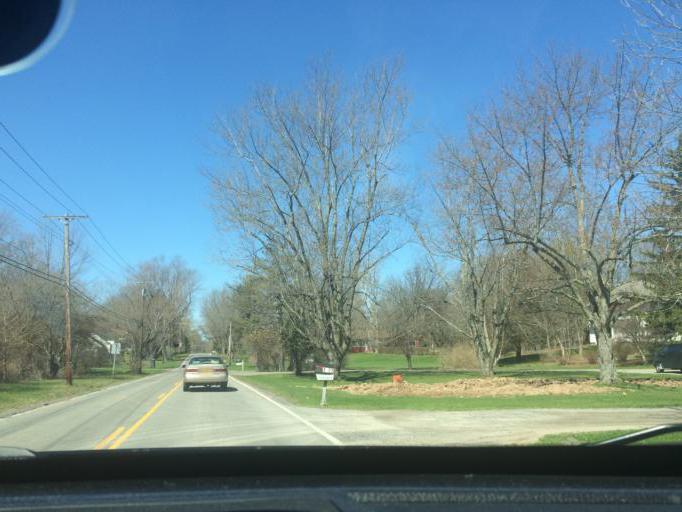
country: US
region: New York
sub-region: Monroe County
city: Rochester
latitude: 43.1040
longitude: -77.6382
